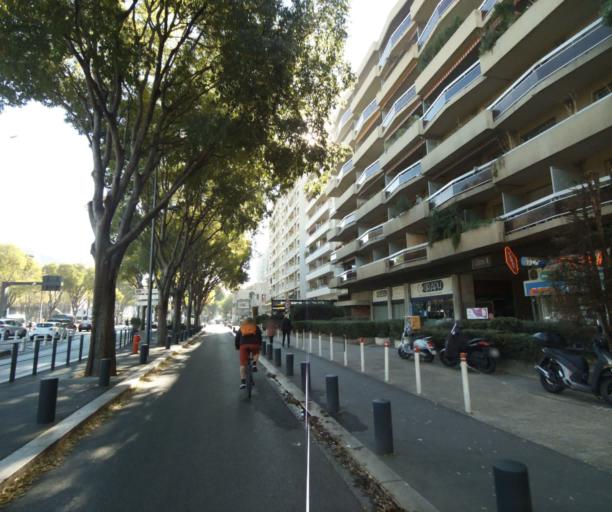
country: FR
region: Provence-Alpes-Cote d'Azur
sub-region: Departement des Bouches-du-Rhone
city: Marseille 08
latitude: 43.2714
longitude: 5.3917
